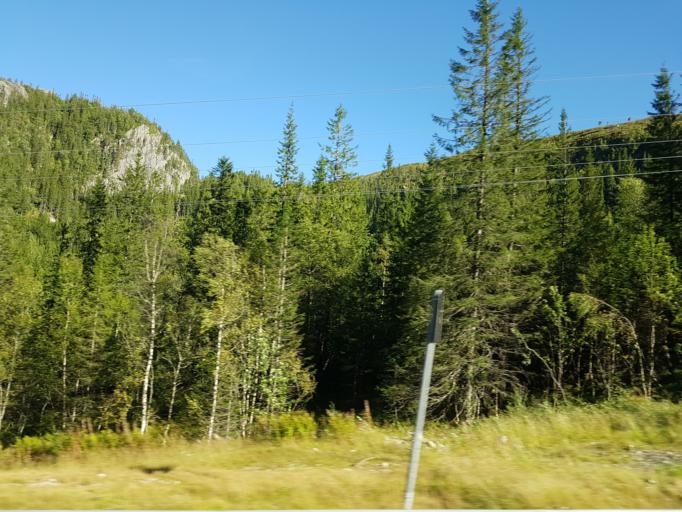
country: NO
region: Sor-Trondelag
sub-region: Afjord
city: A i Afjord
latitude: 63.7731
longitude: 10.2367
